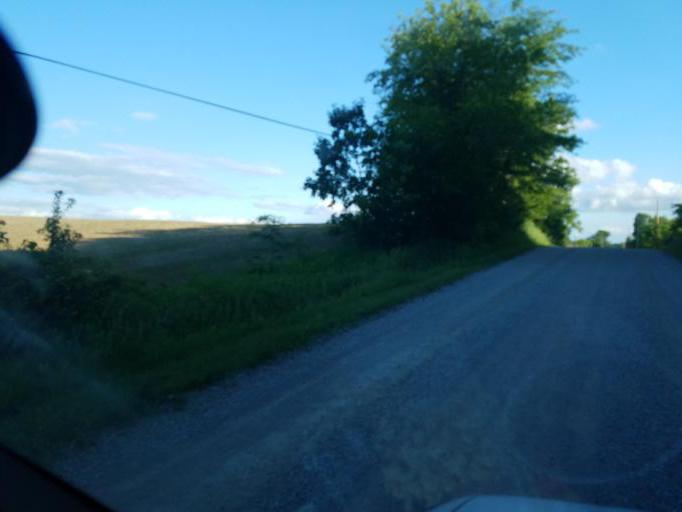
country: US
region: Ohio
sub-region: Morrow County
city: Mount Gilead
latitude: 40.4920
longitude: -82.7189
